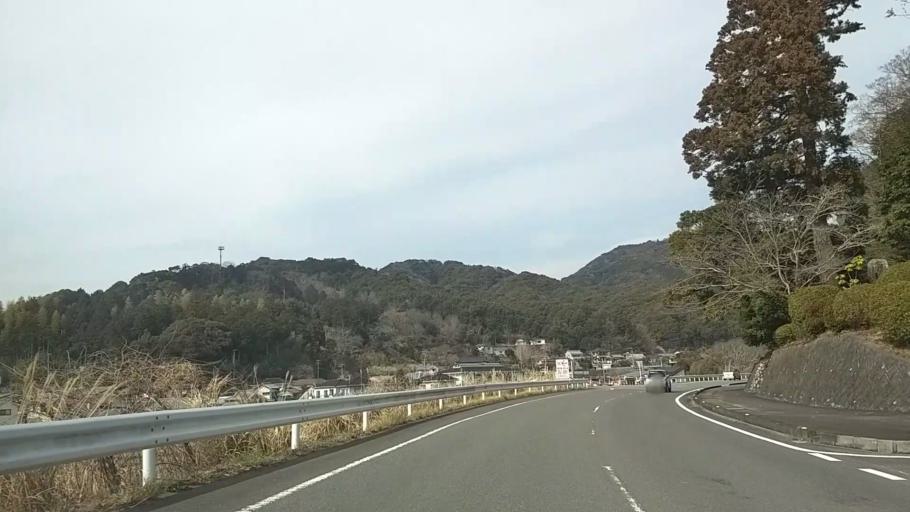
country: JP
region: Shizuoka
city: Shimoda
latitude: 34.7229
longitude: 138.9300
